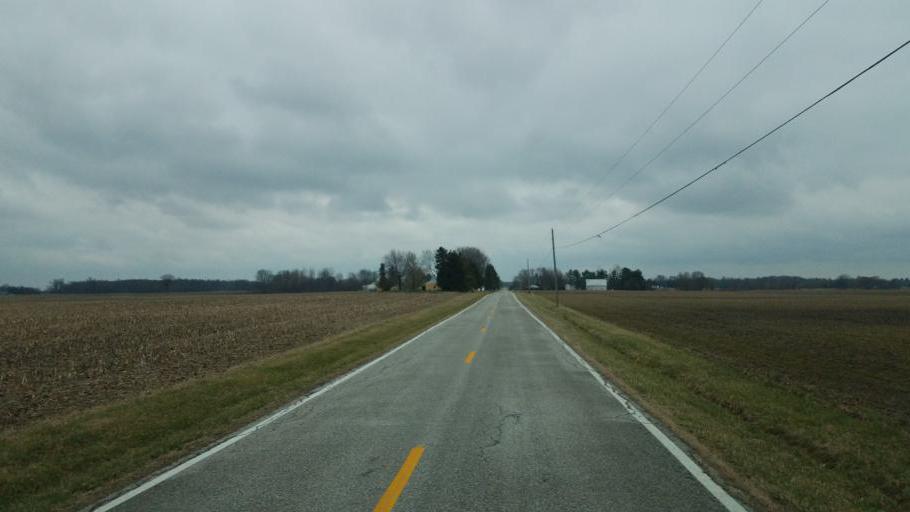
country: US
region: Ohio
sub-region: Delaware County
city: Ashley
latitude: 40.3822
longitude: -83.0148
